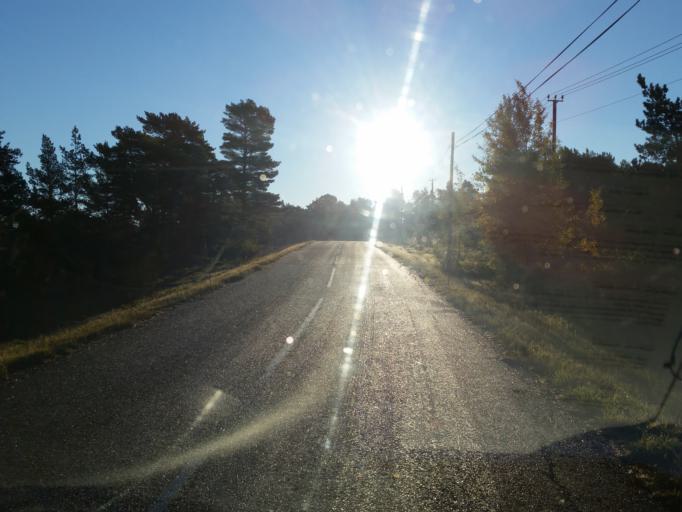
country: AX
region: Alands skaergard
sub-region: Vardoe
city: Vardoe
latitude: 60.3094
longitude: 20.3771
